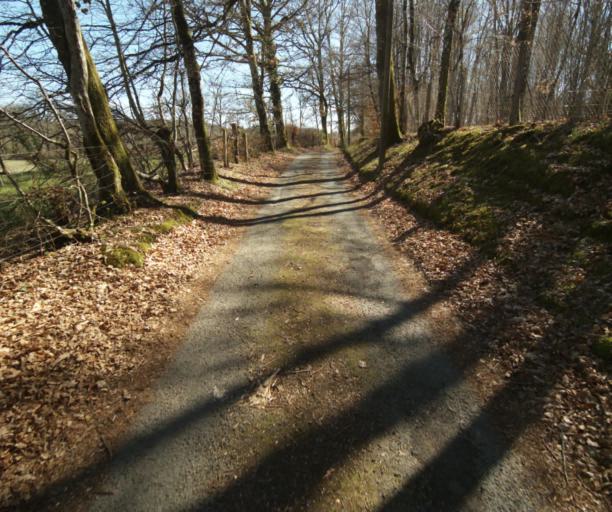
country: FR
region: Limousin
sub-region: Departement de la Correze
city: Chamboulive
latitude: 45.4561
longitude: 1.7289
